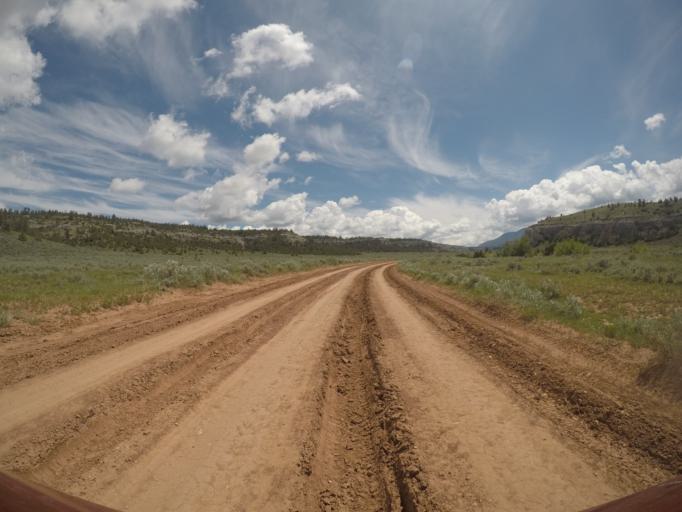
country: US
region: Montana
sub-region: Yellowstone County
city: Laurel
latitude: 45.2436
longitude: -108.6453
